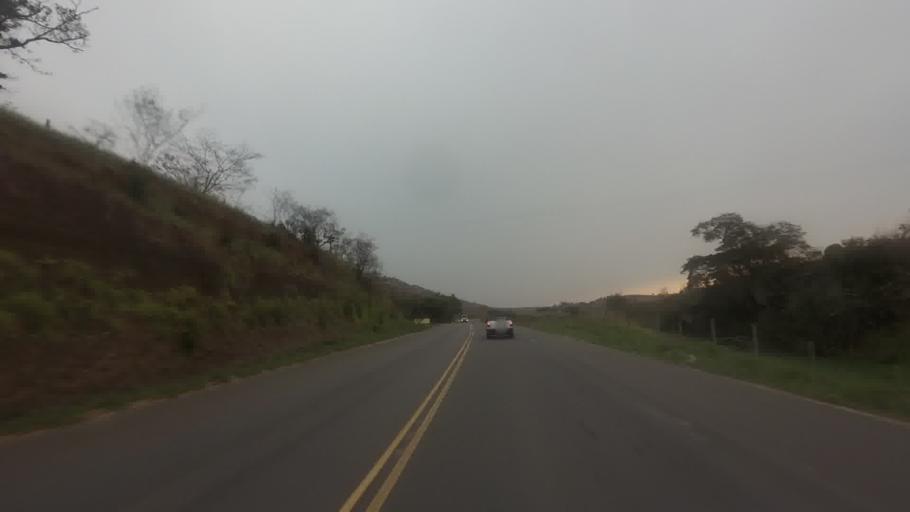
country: BR
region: Minas Gerais
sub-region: Recreio
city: Recreio
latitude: -21.6608
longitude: -42.3760
